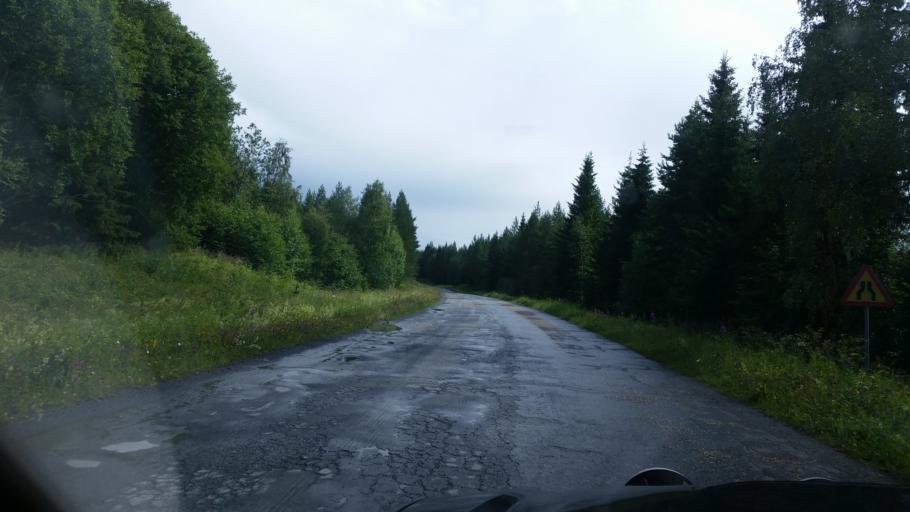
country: SE
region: Jaemtland
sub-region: Krokoms Kommun
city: Krokom
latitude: 63.3212
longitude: 14.3042
